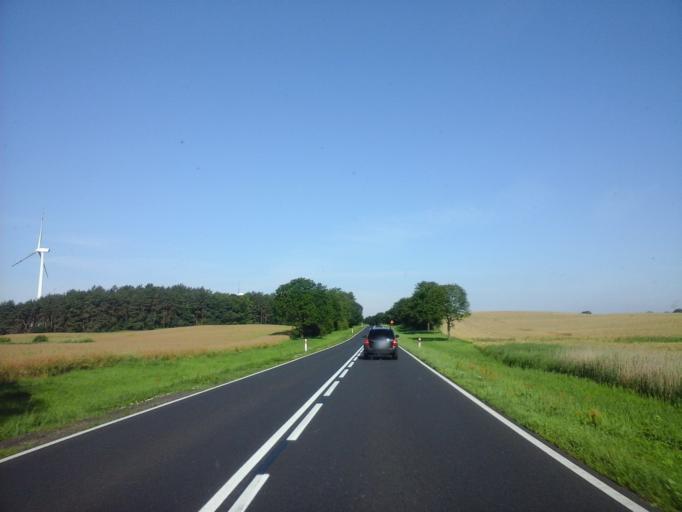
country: PL
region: West Pomeranian Voivodeship
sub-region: Powiat stargardzki
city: Suchan
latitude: 53.2865
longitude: 15.2584
